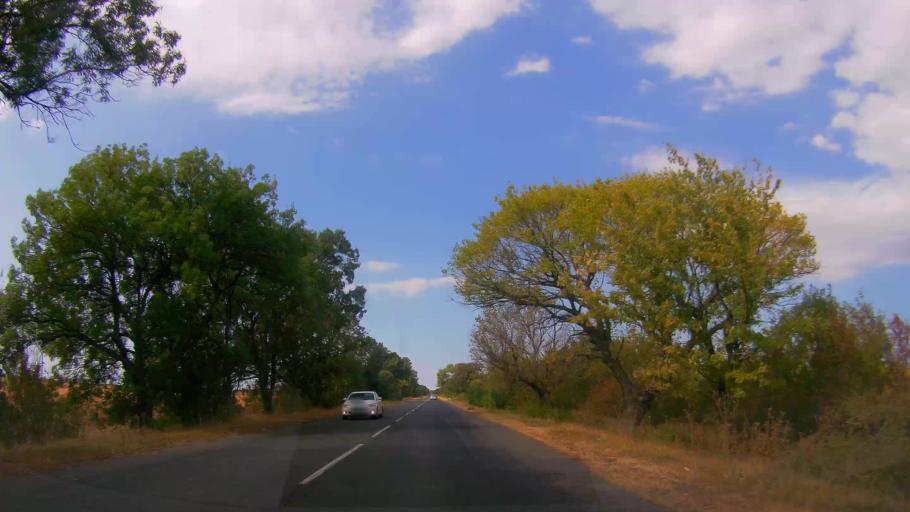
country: BG
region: Burgas
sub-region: Obshtina Aytos
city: Aytos
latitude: 42.6890
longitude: 27.1537
